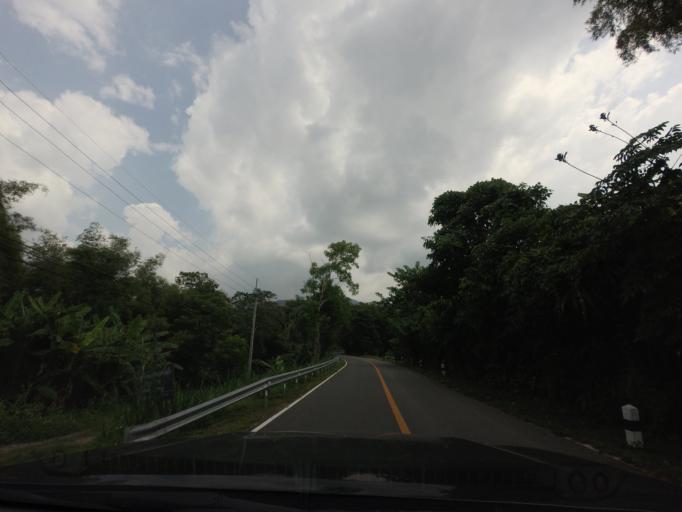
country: TH
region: Nan
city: Pua
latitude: 19.1796
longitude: 100.9620
